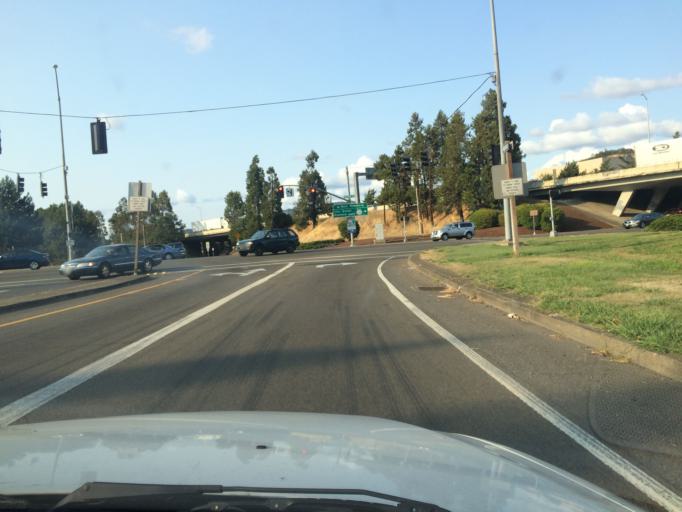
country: US
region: Oregon
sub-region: Douglas County
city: Roseburg
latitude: 43.2134
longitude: -123.3564
